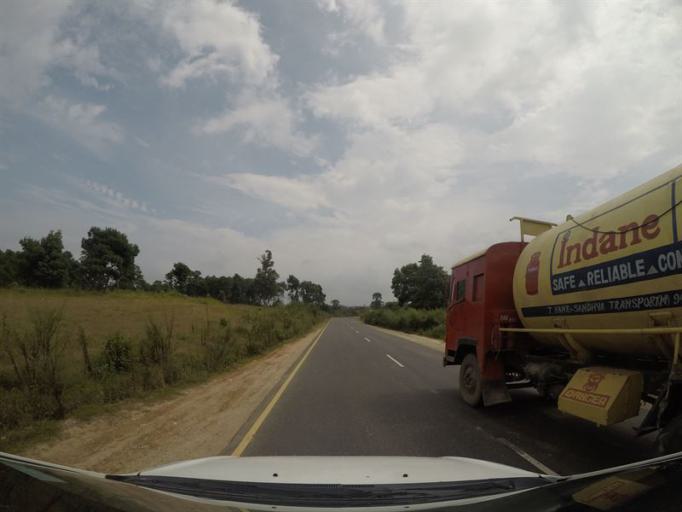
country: IN
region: Meghalaya
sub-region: East Khasi Hills
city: Shillong
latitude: 25.4887
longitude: 92.1907
